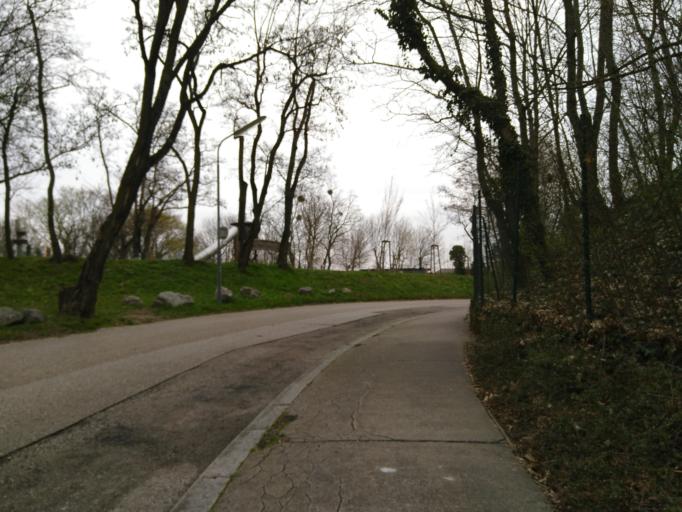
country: AT
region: Lower Austria
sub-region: Politischer Bezirk Modling
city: Perchtoldsdorf
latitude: 48.1799
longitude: 16.2888
